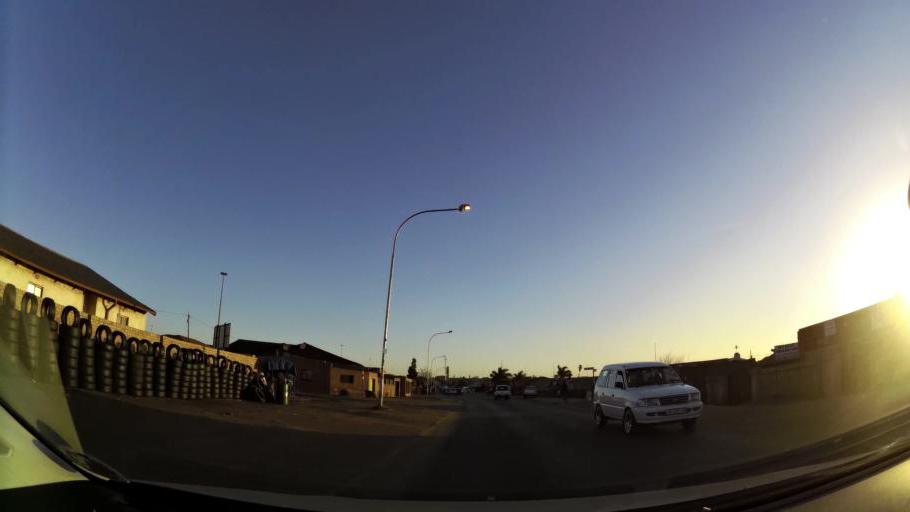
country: ZA
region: Gauteng
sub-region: Ekurhuleni Metropolitan Municipality
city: Tembisa
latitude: -25.9965
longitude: 28.2203
